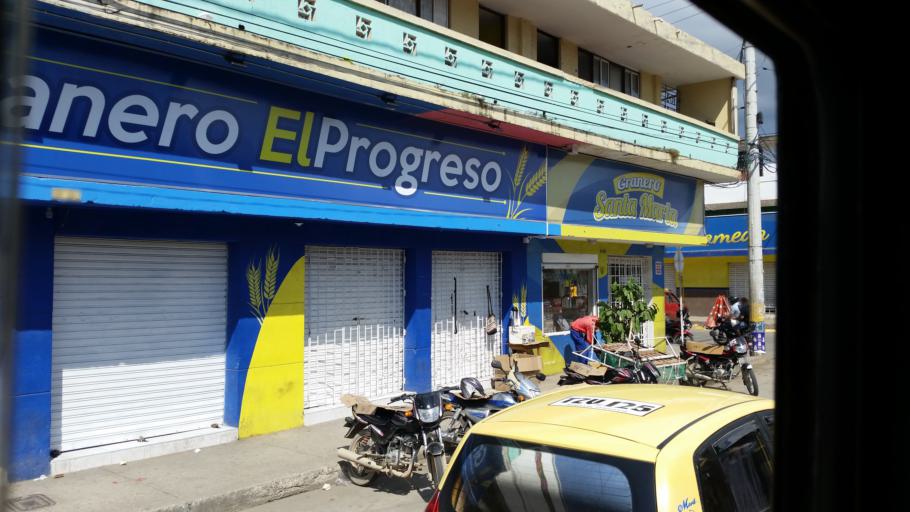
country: CO
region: Magdalena
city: Santa Marta
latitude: 11.2457
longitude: -74.2055
